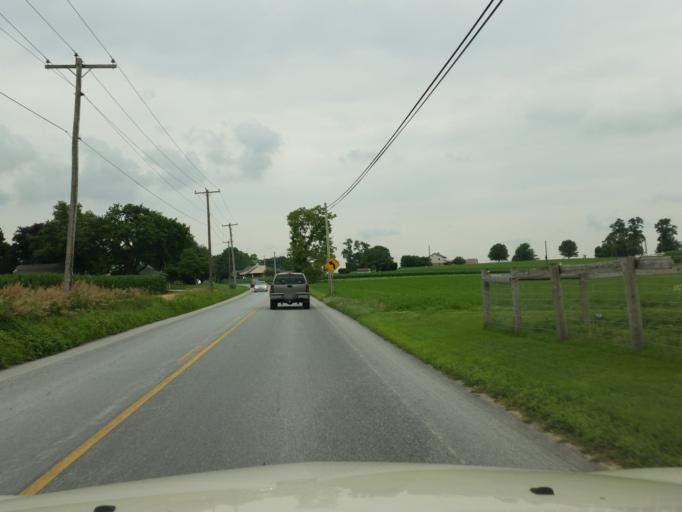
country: US
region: Pennsylvania
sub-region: Lancaster County
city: Strasburg
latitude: 39.9995
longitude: -76.2084
